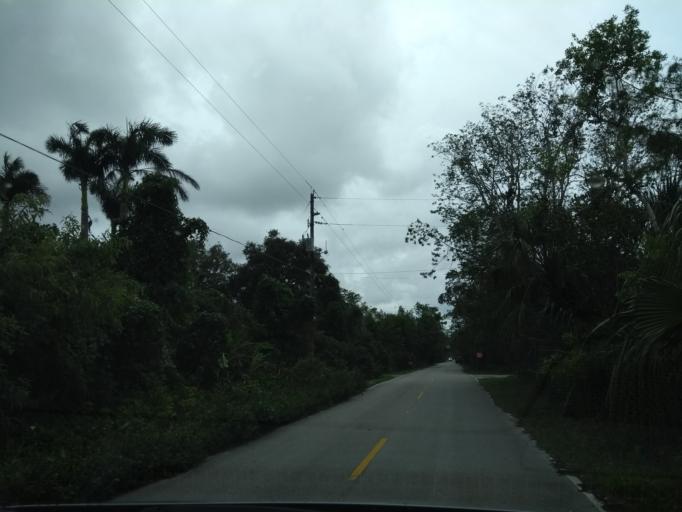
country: US
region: Florida
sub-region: Miami-Dade County
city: The Hammocks
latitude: 25.7464
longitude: -80.9462
